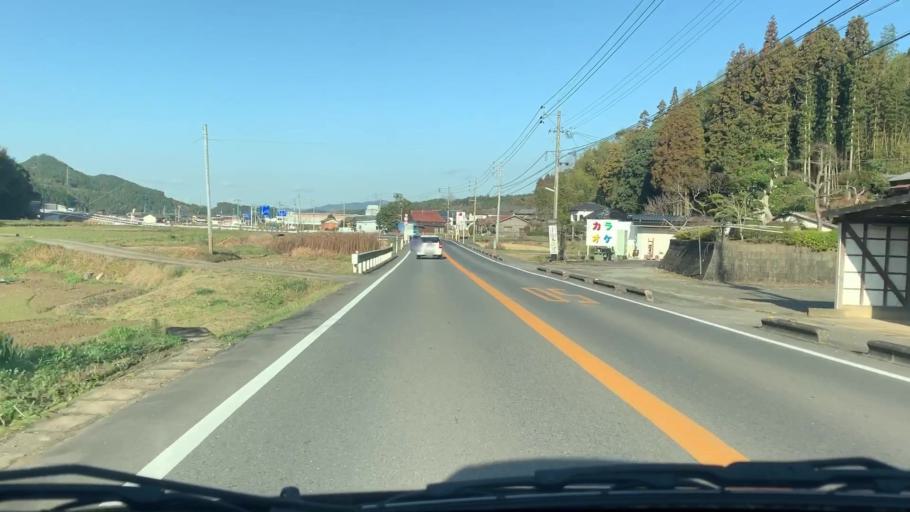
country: JP
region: Saga Prefecture
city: Takeocho-takeo
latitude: 33.2489
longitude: 130.0017
